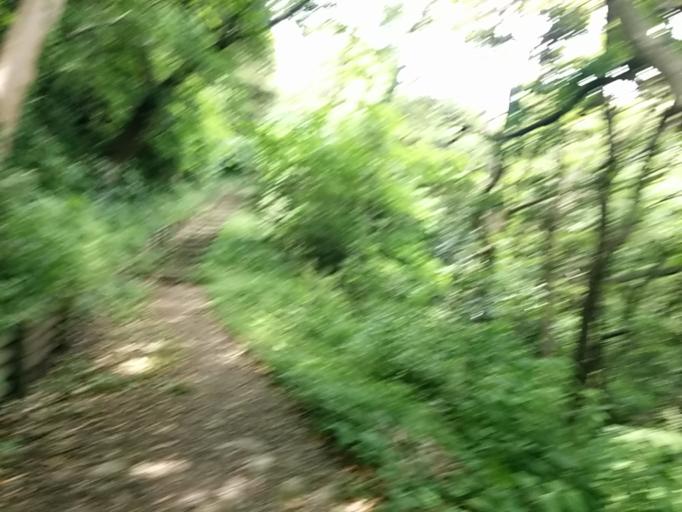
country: JP
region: Kyoto
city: Miyazu
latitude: 35.7761
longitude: 135.2234
